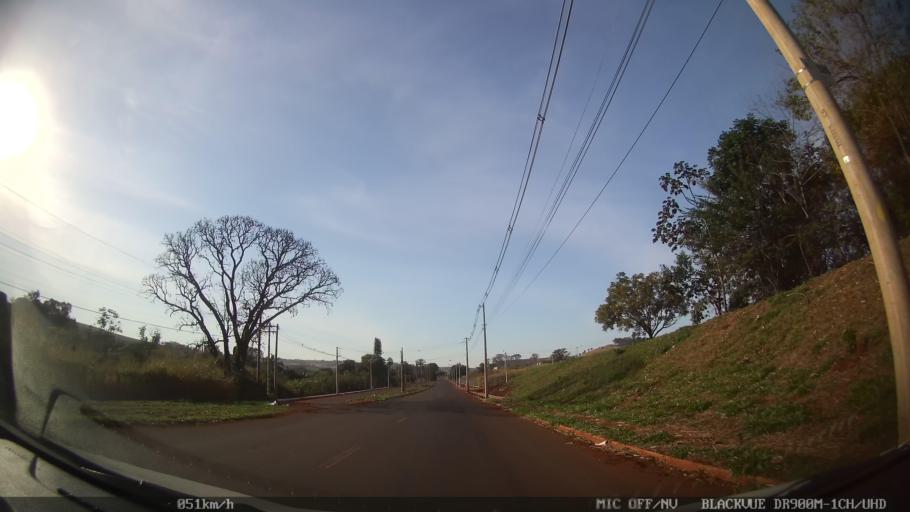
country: BR
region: Sao Paulo
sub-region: Ribeirao Preto
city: Ribeirao Preto
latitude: -21.2736
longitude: -47.8120
